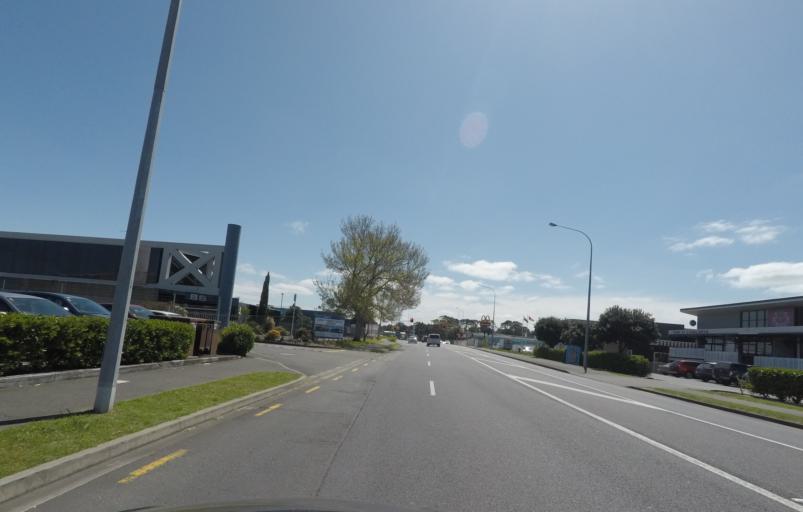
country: NZ
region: Auckland
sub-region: Auckland
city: Tamaki
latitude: -36.8904
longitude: 174.8338
